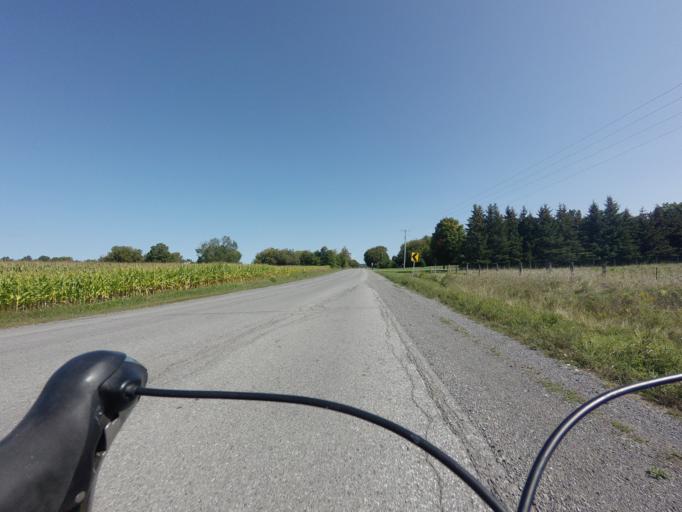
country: CA
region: Ontario
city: Carleton Place
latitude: 45.3312
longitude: -76.0862
